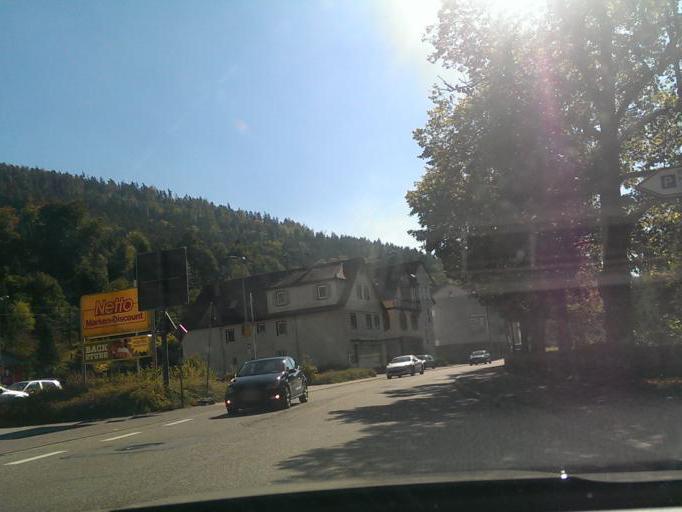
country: DE
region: Baden-Wuerttemberg
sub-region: Karlsruhe Region
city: Hofen an der Enz
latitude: 48.8015
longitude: 8.5833
